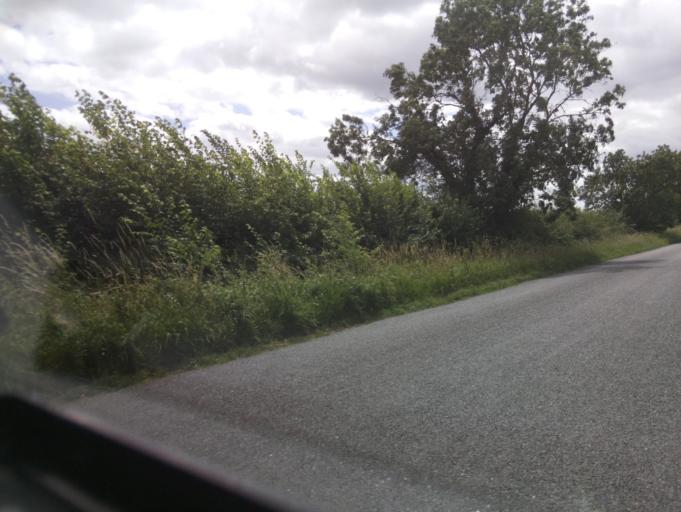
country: GB
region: England
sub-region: Nottinghamshire
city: Ruddington
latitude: 52.8653
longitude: -1.0940
